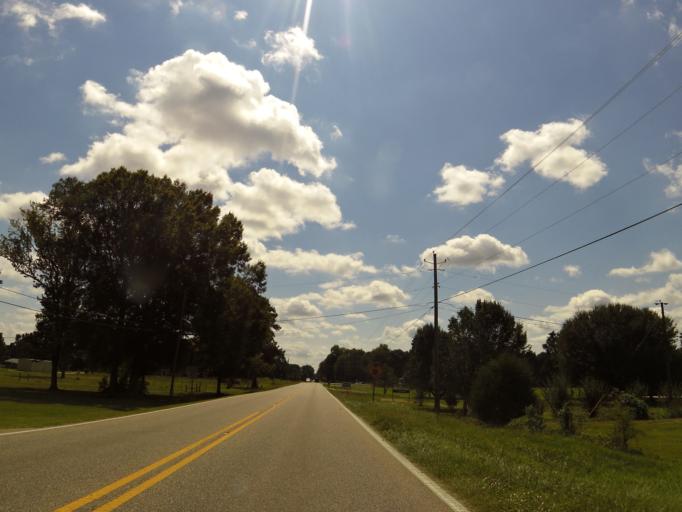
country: US
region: Alabama
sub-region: Dallas County
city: Selma
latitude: 32.4230
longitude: -87.0833
